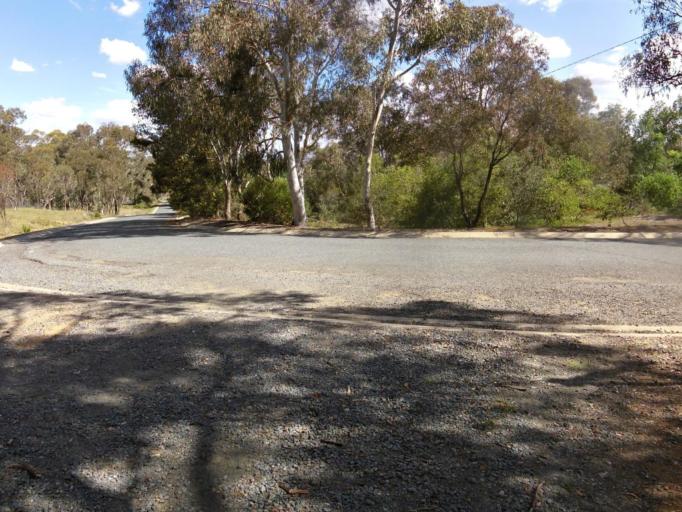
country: AU
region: Australian Capital Territory
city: Belconnen
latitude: -35.1663
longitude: 149.0706
